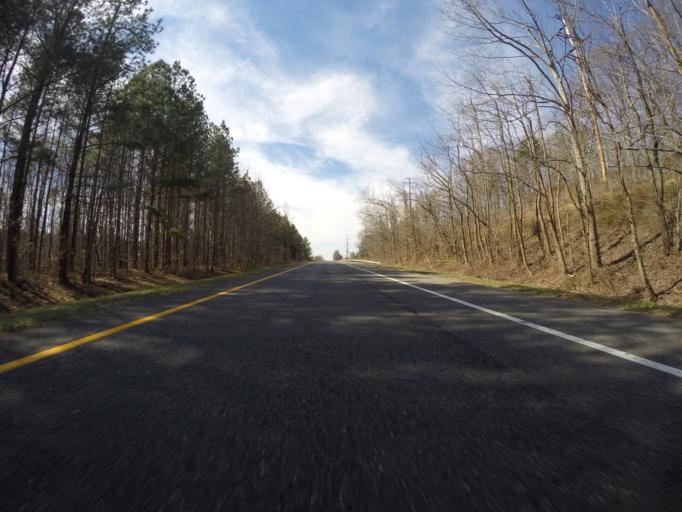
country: US
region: Maryland
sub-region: Anne Arundel County
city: Crownsville
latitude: 39.0442
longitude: -76.6139
